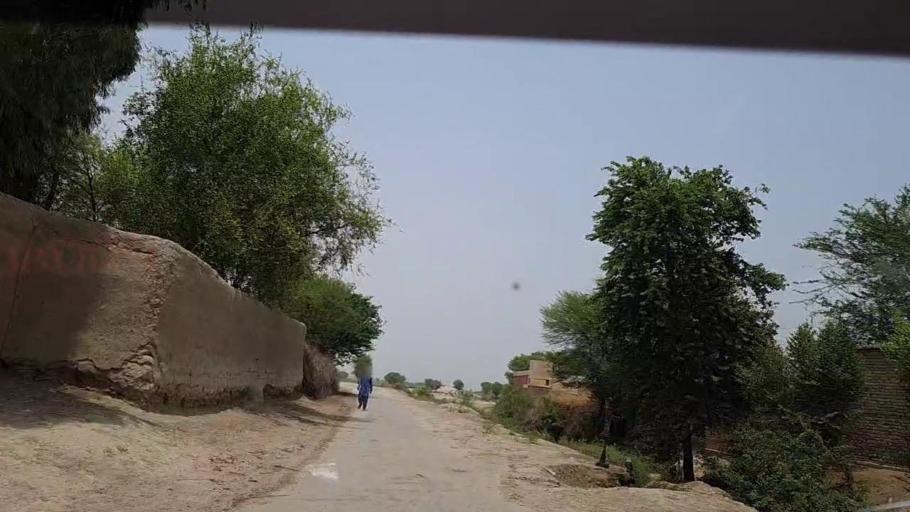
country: PK
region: Sindh
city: Khairpur Nathan Shah
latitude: 27.0222
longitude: 67.6693
